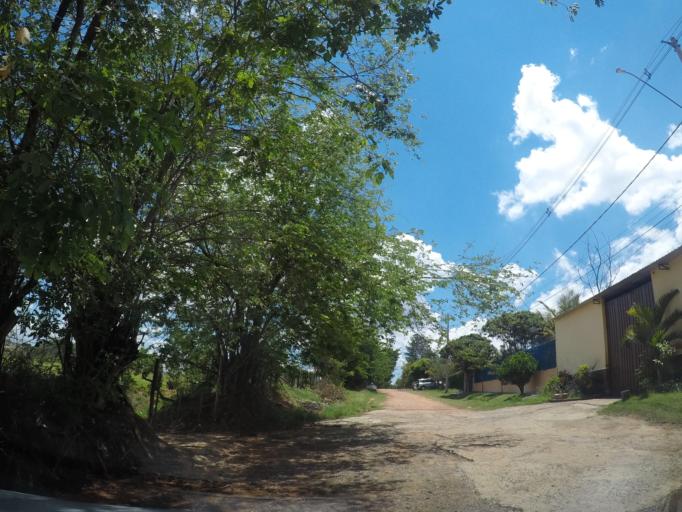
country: BR
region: Sao Paulo
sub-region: Hortolandia
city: Hortolandia
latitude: -22.8426
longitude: -47.2275
